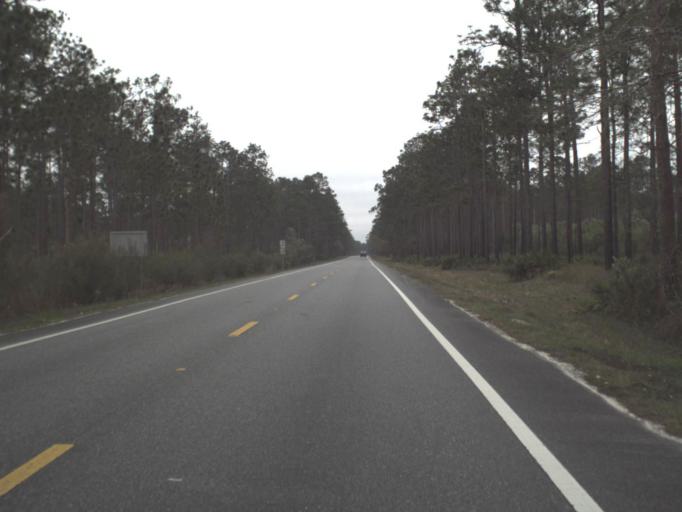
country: US
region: Florida
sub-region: Gulf County
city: Wewahitchka
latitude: 29.9919
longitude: -84.9767
